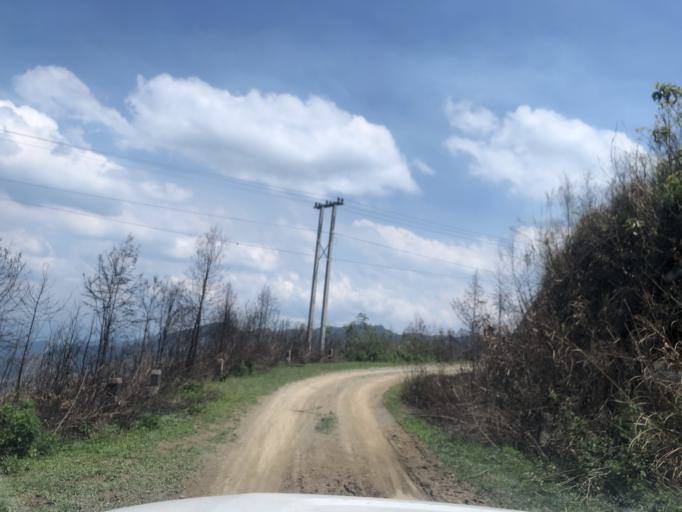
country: LA
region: Phongsali
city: Phongsali
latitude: 21.4102
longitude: 102.1868
